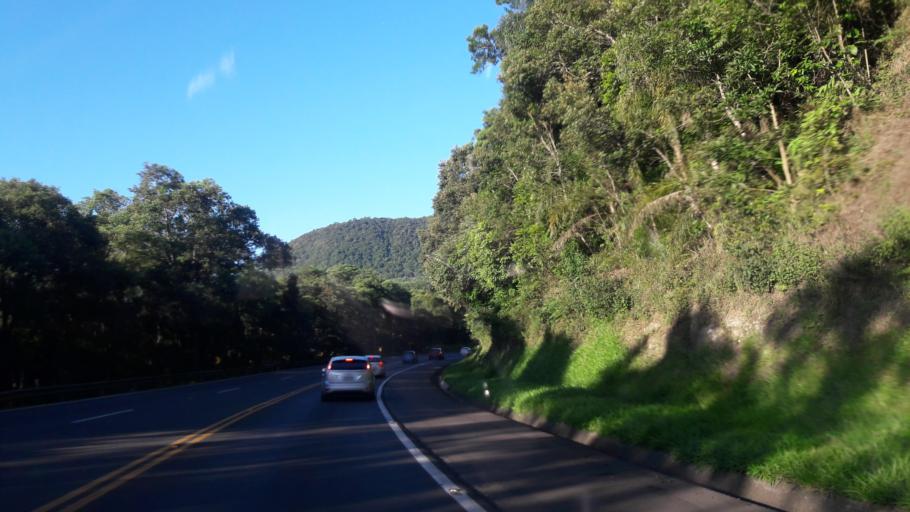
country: BR
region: Parana
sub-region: Prudentopolis
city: Prudentopolis
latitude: -25.3145
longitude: -51.1882
